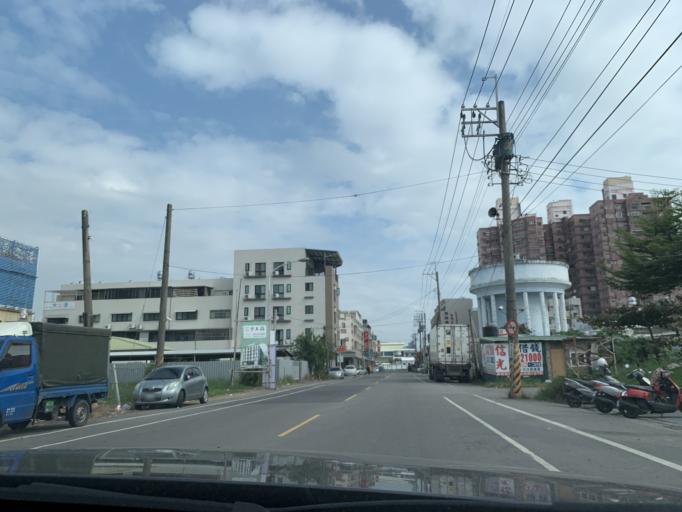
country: TW
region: Taiwan
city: Fengshan
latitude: 22.4667
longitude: 120.4611
